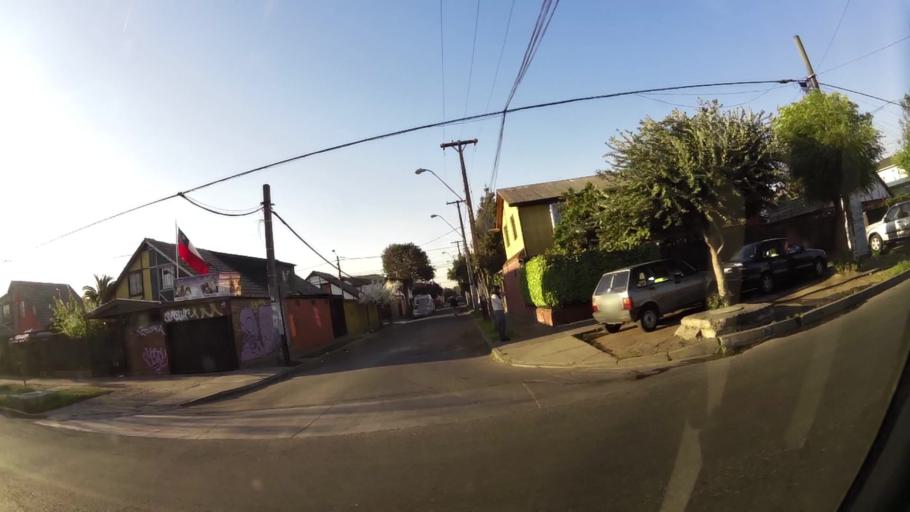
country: CL
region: Santiago Metropolitan
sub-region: Provincia de Santiago
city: Lo Prado
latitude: -33.4748
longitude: -70.7471
